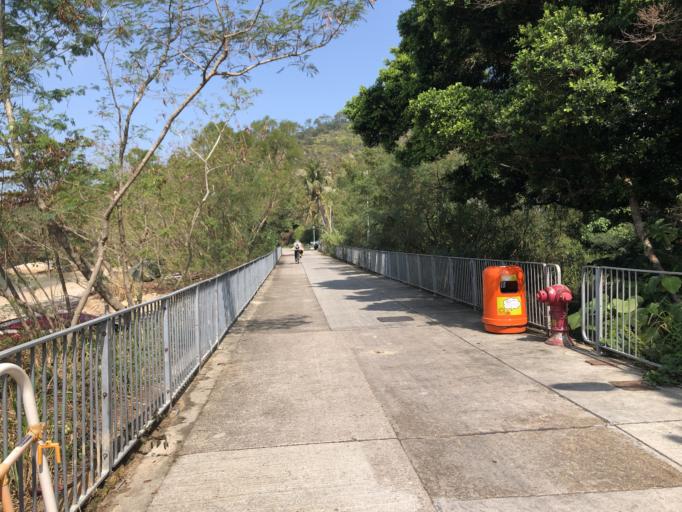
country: HK
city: Yung Shue Wan
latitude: 22.2166
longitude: 114.0266
